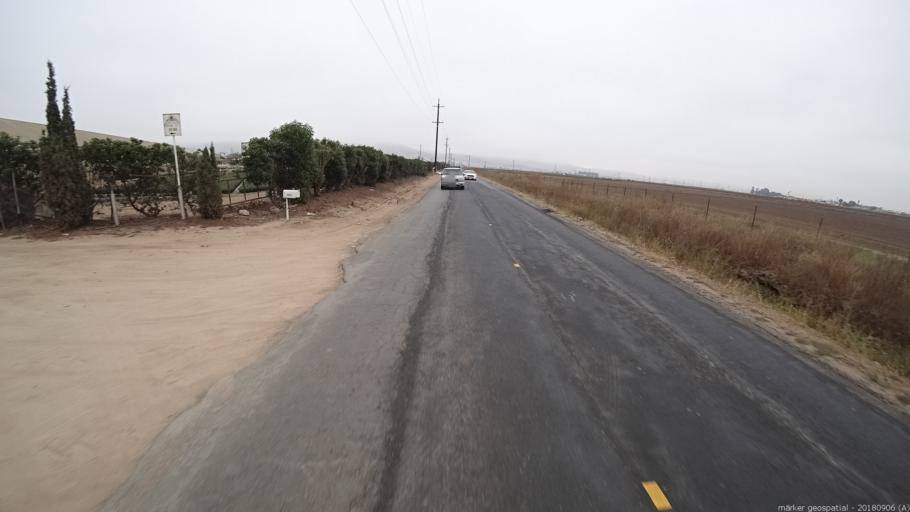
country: US
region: California
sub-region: Monterey County
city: Chualar
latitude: 36.6274
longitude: -121.5439
